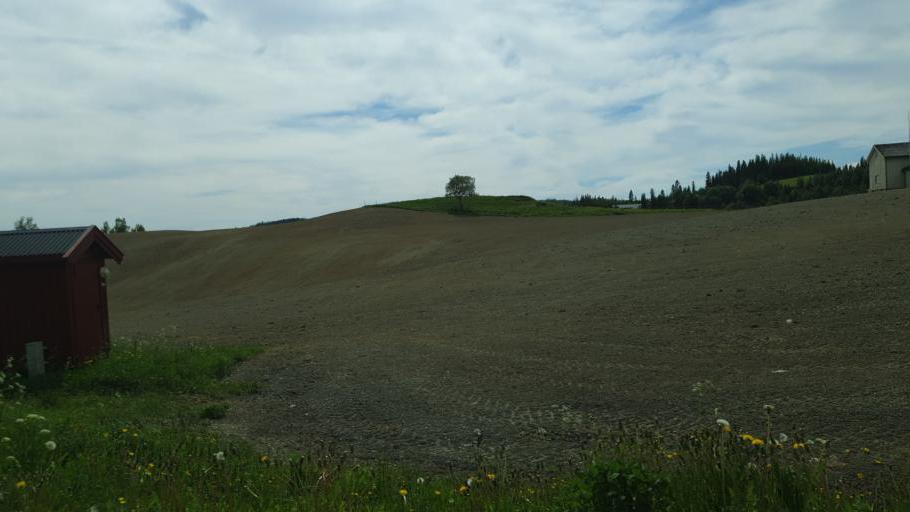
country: NO
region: Nord-Trondelag
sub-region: Leksvik
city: Leksvik
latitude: 63.6855
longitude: 10.5685
